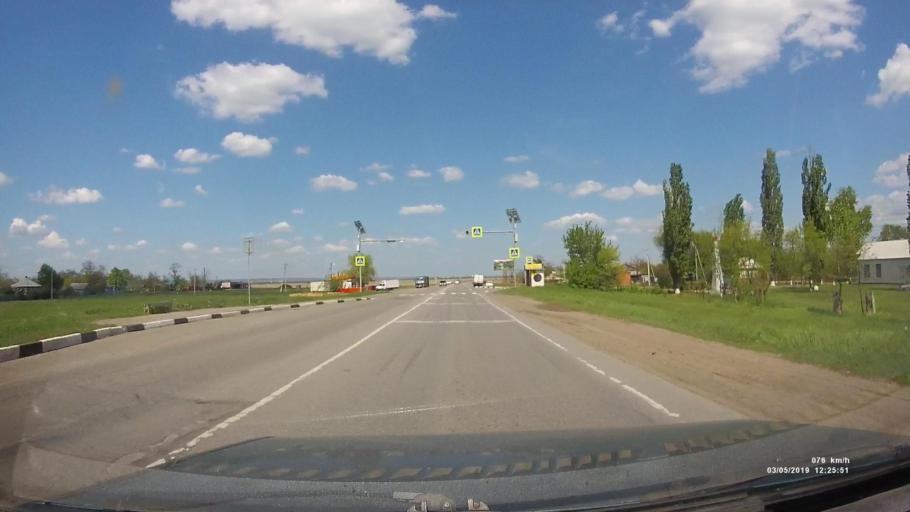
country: RU
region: Rostov
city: Semikarakorsk
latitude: 47.4381
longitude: 40.7119
